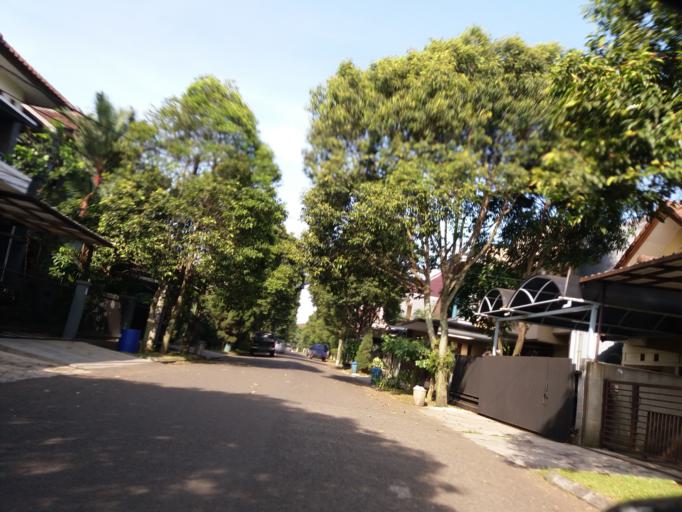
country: ID
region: West Java
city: Bandung
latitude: -6.9618
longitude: 107.6306
